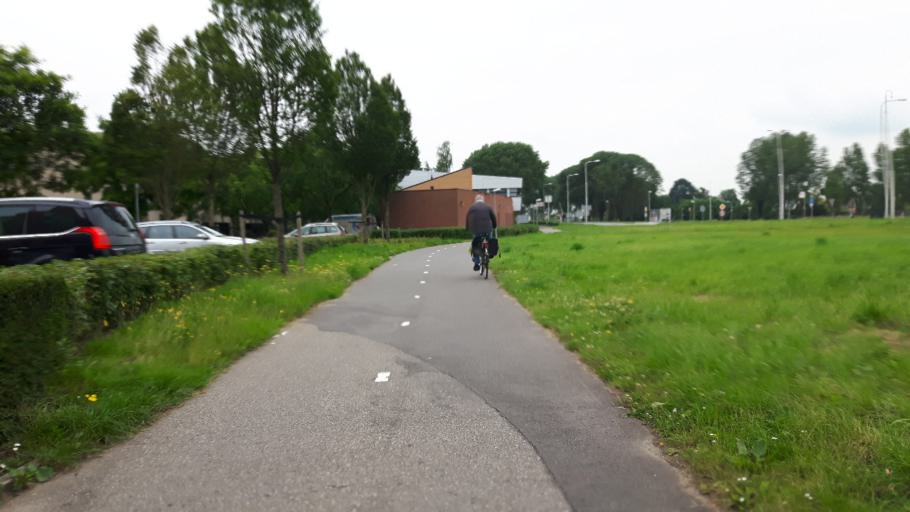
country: NL
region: South Holland
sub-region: Gemeente Schoonhoven
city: Schoonhoven
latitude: 51.9477
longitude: 4.8592
